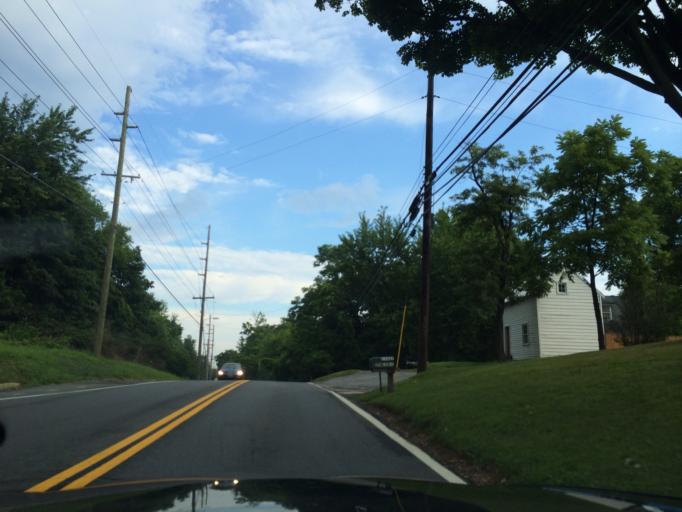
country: US
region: Maryland
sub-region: Montgomery County
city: Clarksburg
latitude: 39.2411
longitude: -77.2823
